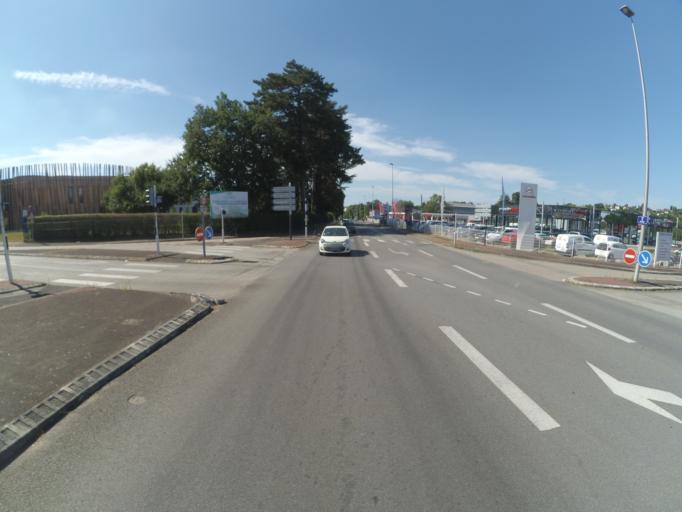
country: FR
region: Limousin
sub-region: Departement de la Haute-Vienne
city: Condat-sur-Vienne
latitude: 45.8182
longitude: 1.2872
